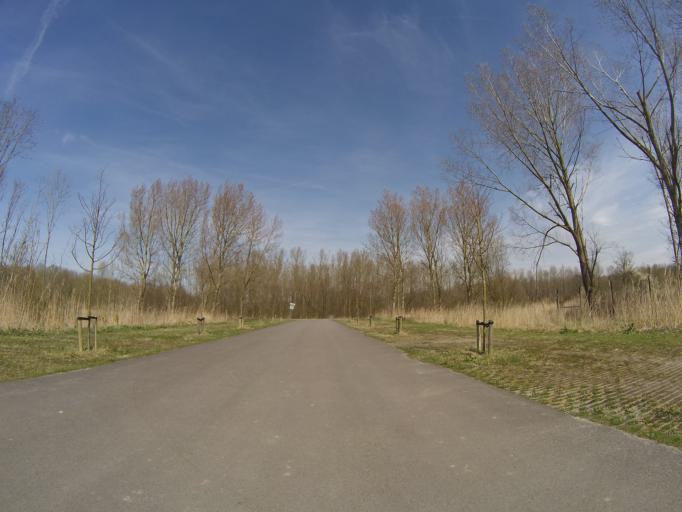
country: NL
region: Flevoland
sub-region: Gemeente Zeewolde
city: Zeewolde
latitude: 52.3151
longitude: 5.4694
